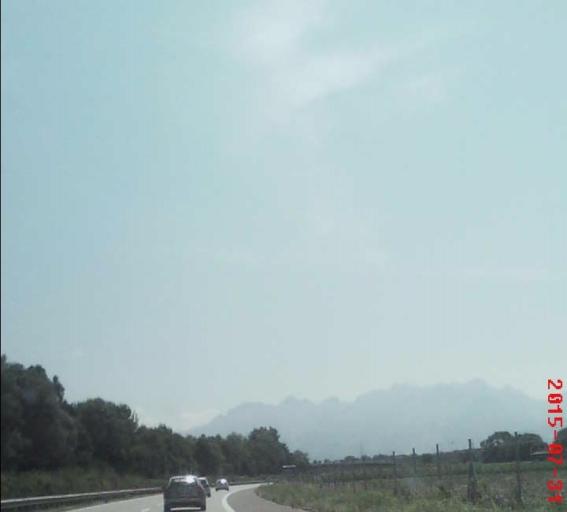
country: AT
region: Vorarlberg
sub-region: Politischer Bezirk Feldkirch
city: Koblach
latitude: 47.3195
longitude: 9.5859
